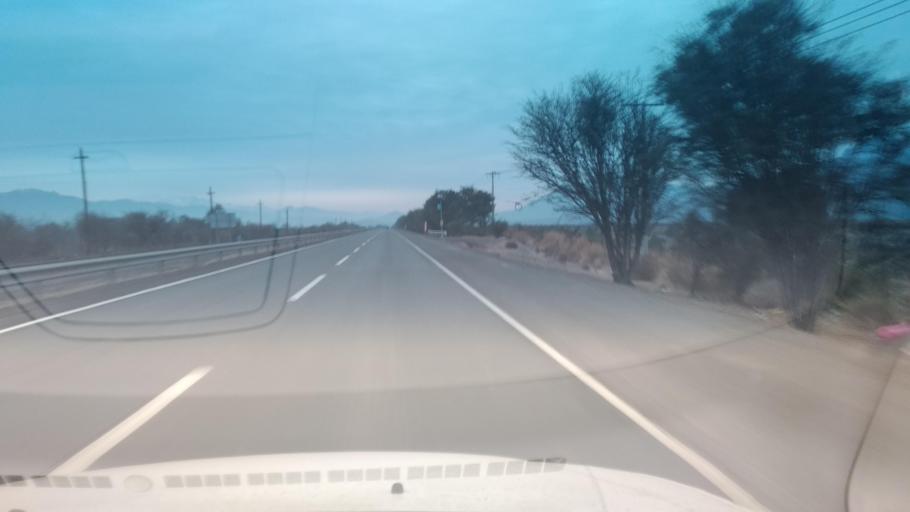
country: CL
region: Santiago Metropolitan
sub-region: Provincia de Chacabuco
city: Chicureo Abajo
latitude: -33.1001
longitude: -70.6915
